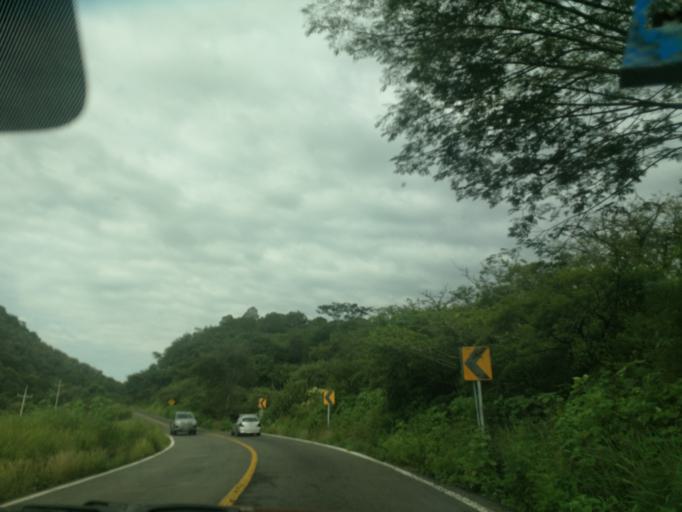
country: MX
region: Jalisco
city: Ameca
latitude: 20.5436
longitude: -104.2795
